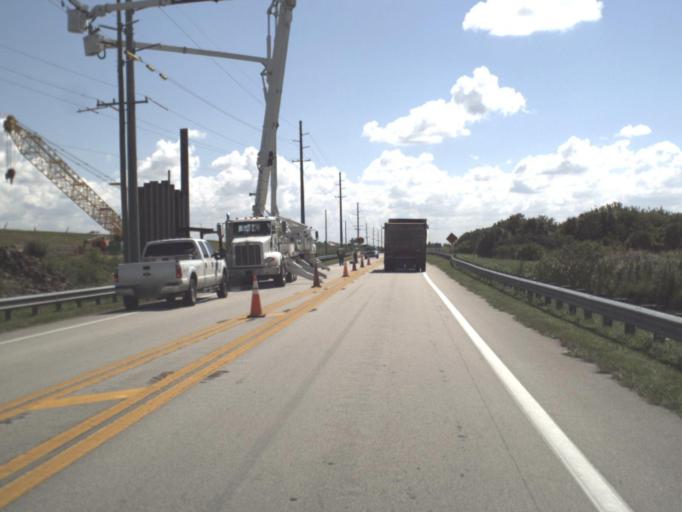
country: US
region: Florida
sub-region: Glades County
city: Moore Haven
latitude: 26.8871
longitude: -81.1226
